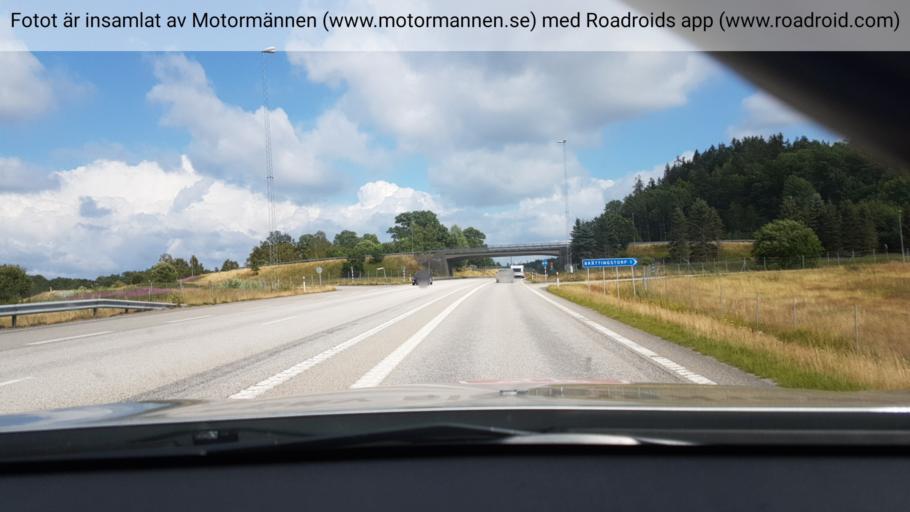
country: SE
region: Vaestra Goetaland
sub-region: Marks Kommun
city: Kinna
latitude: 57.5126
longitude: 12.7333
